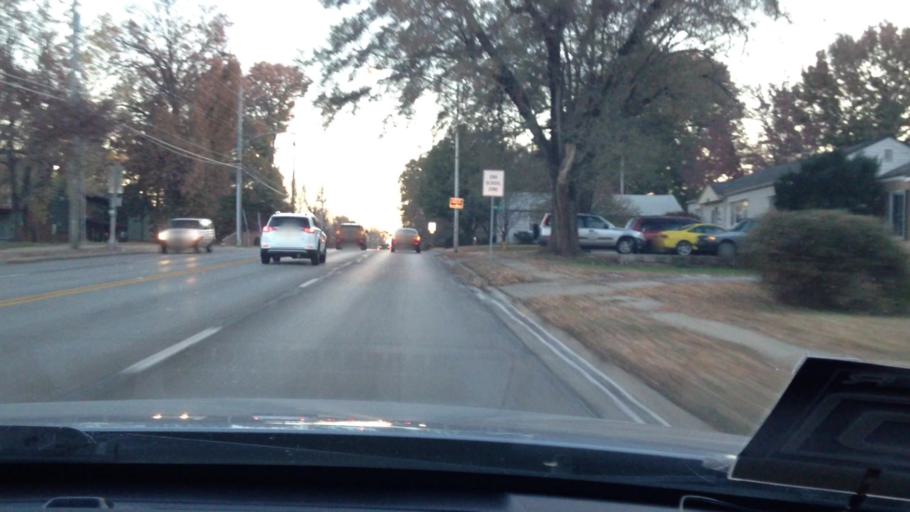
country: US
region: Kansas
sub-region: Johnson County
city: Merriam
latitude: 39.0062
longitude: -94.7145
